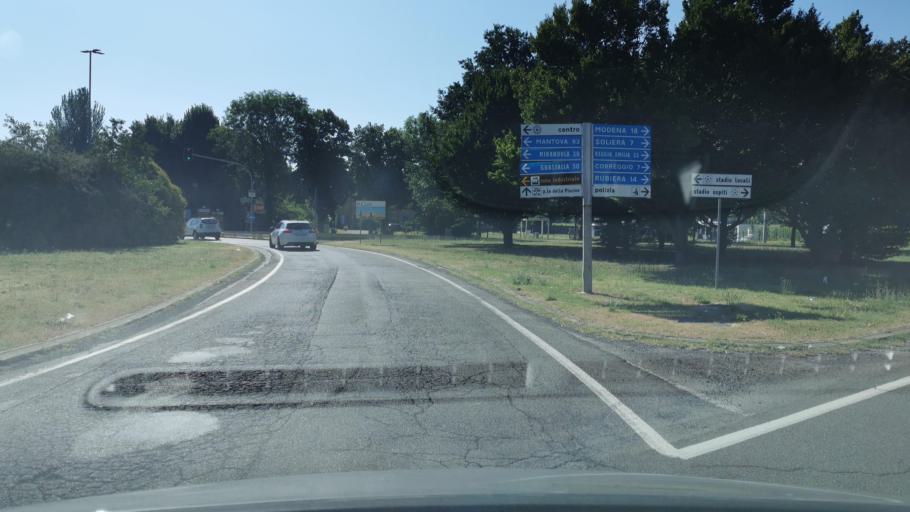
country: IT
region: Emilia-Romagna
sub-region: Provincia di Modena
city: Santa Croce Scuole
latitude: 44.7675
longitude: 10.8497
